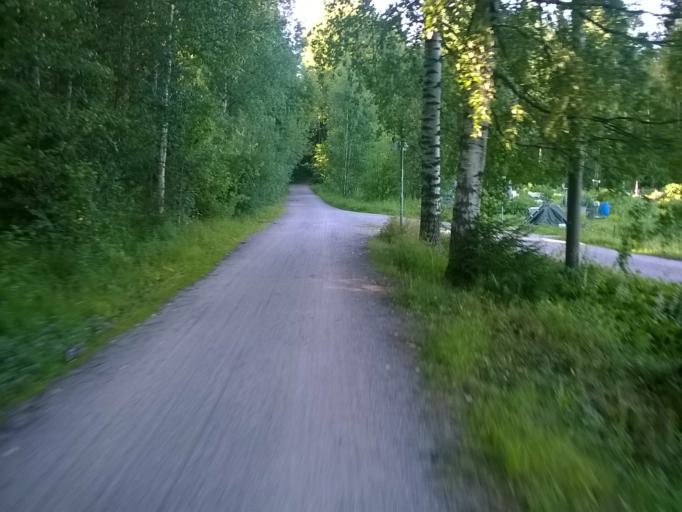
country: FI
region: Uusimaa
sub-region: Helsinki
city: Helsinki
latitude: 60.2257
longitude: 24.9137
